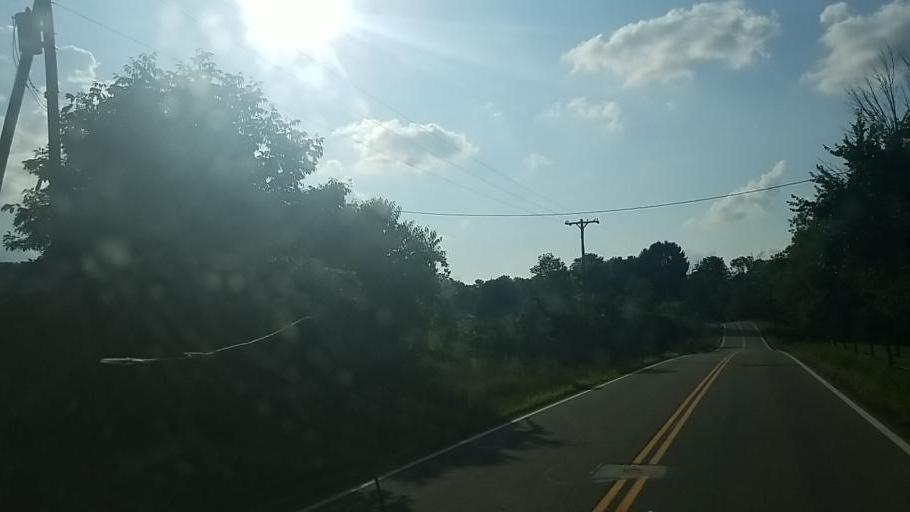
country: US
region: Ohio
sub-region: Wayne County
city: West Salem
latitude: 40.9034
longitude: -82.1689
